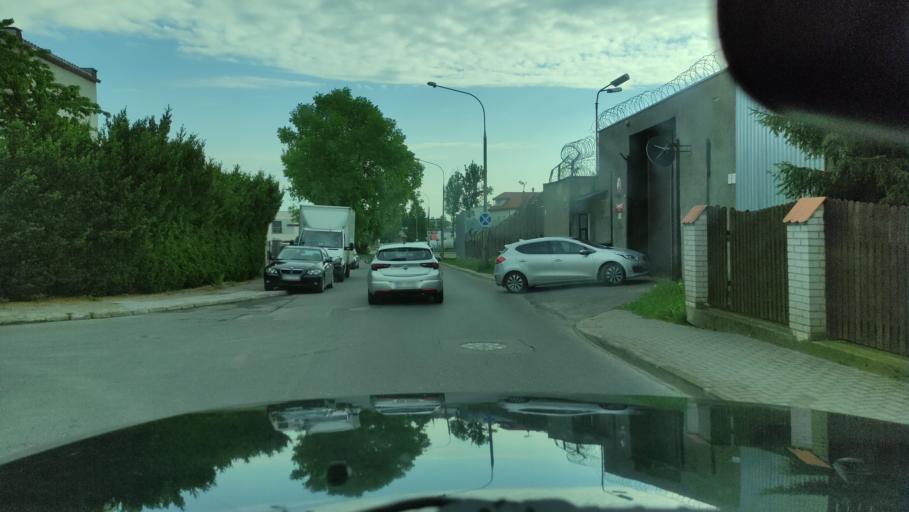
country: PL
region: Warmian-Masurian Voivodeship
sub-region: Powiat olsztynski
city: Olsztyn
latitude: 53.7655
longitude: 20.5089
